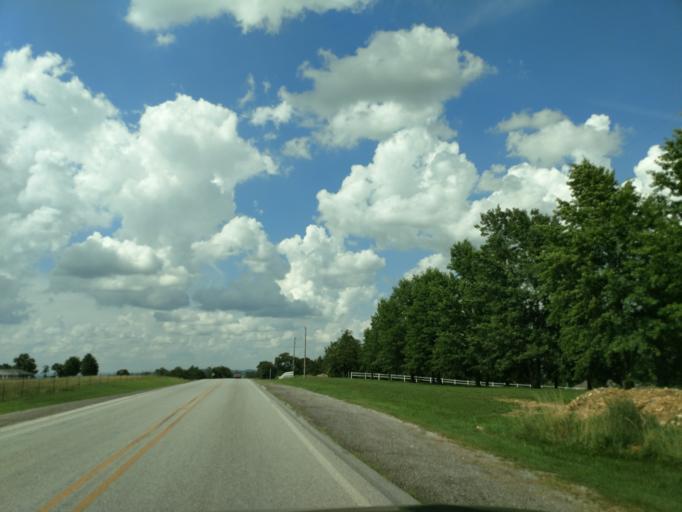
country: US
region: Arkansas
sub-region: Carroll County
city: Berryville
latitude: 36.4366
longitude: -93.5563
